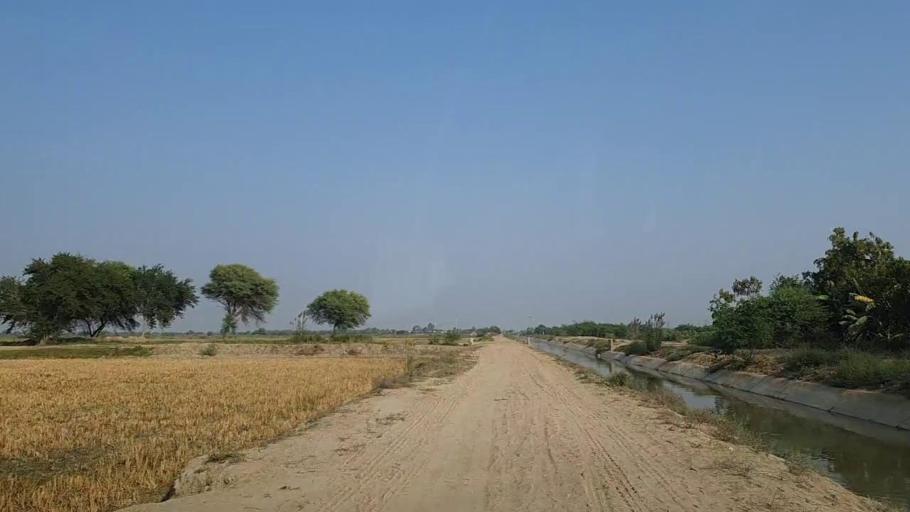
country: PK
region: Sindh
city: Mirpur Sakro
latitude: 24.6155
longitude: 67.7206
